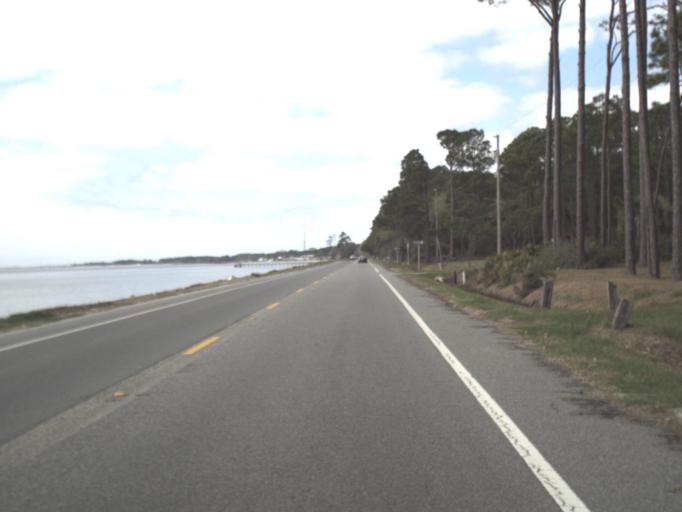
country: US
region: Florida
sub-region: Franklin County
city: Eastpoint
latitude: 29.7489
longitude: -84.8530
